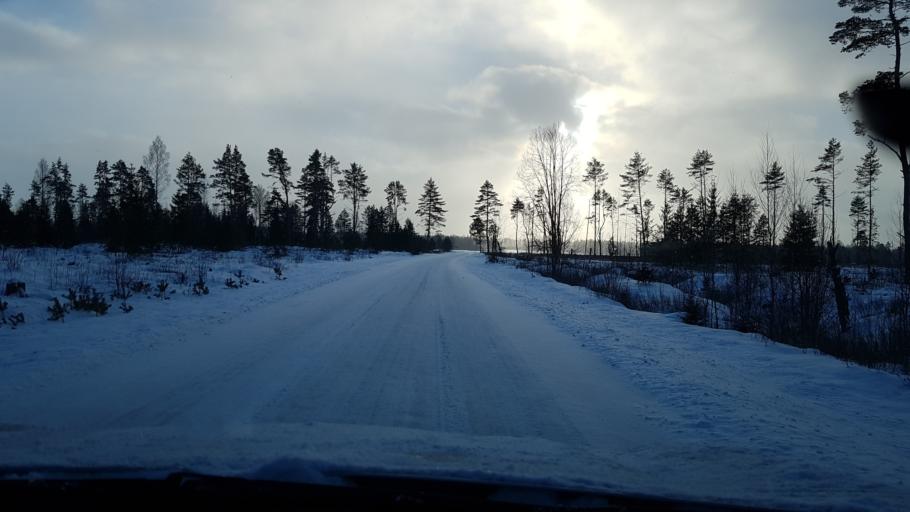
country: EE
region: Harju
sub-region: Nissi vald
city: Turba
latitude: 59.2087
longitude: 24.1409
